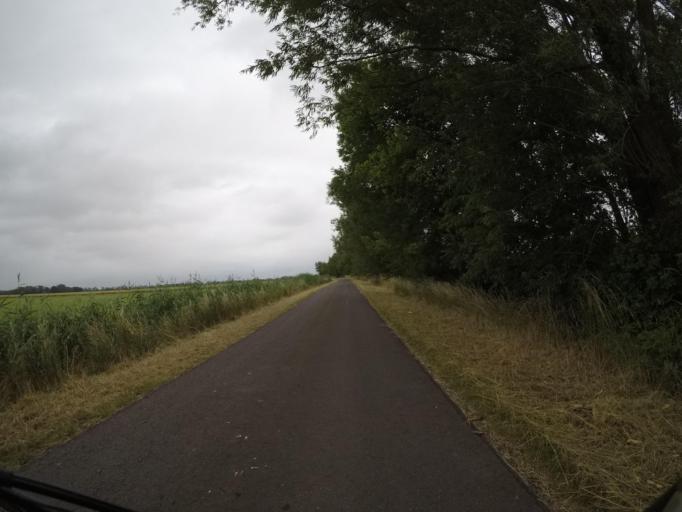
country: DE
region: Lower Saxony
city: Hitzacker
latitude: 53.1751
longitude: 11.0847
